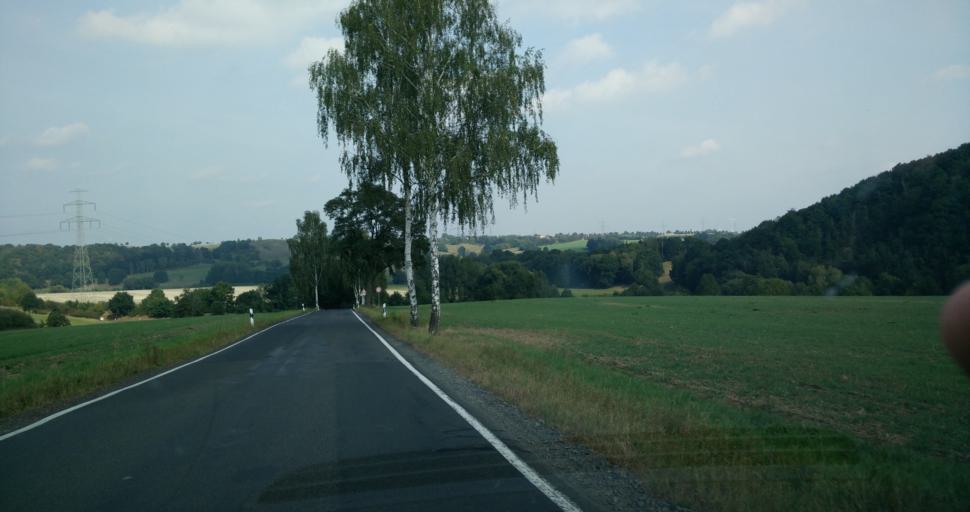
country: DE
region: Saxony
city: Colditz
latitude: 51.1049
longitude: 12.8040
